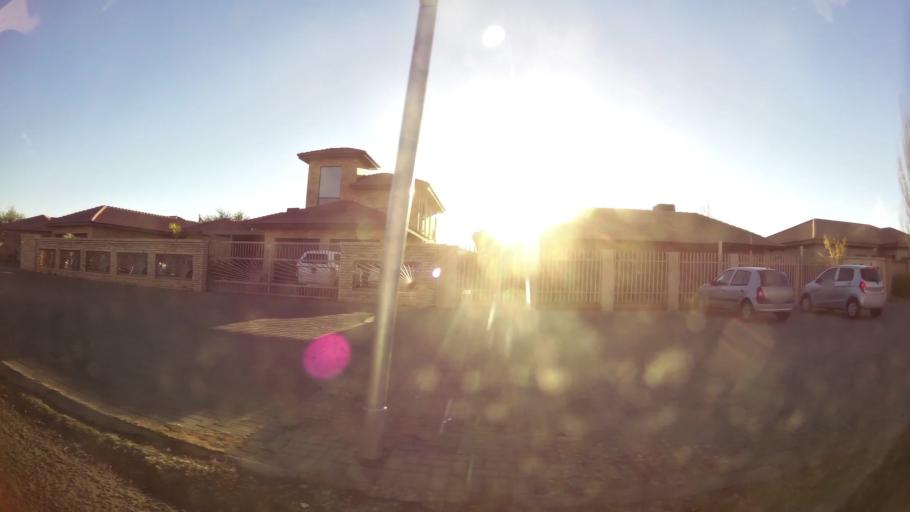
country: ZA
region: Northern Cape
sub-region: Frances Baard District Municipality
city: Kimberley
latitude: -28.7574
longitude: 24.7398
